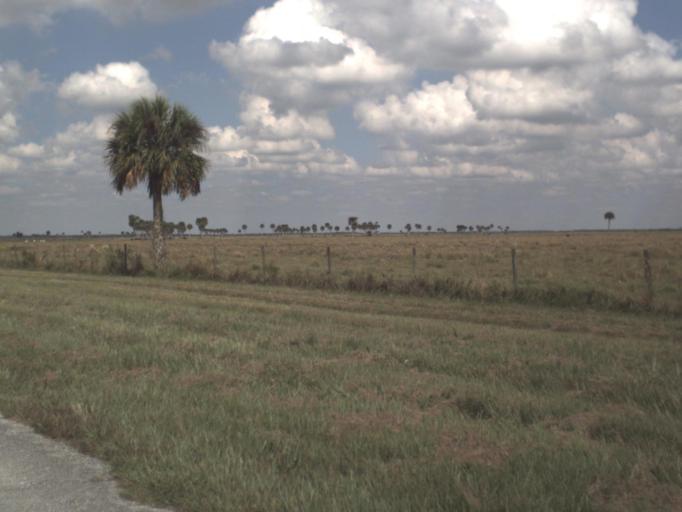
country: US
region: Florida
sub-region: Okeechobee County
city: Okeechobee
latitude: 27.3364
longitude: -80.9354
